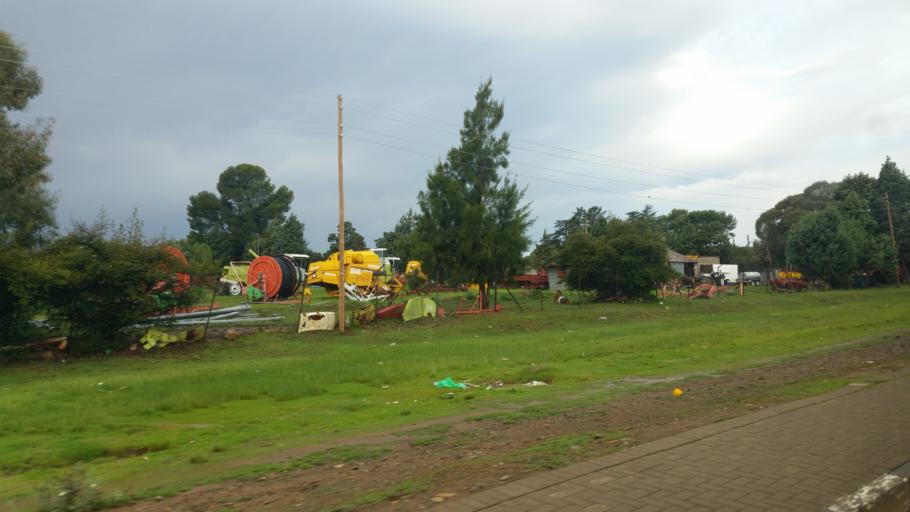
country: LS
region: Mafeteng
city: Mafeteng
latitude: -29.8186
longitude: 27.2366
